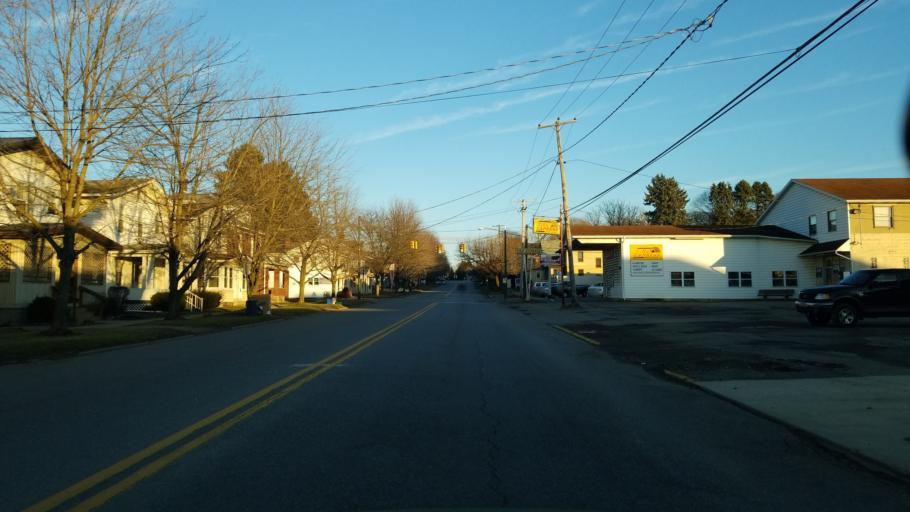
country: US
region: Pennsylvania
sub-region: Indiana County
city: Indiana
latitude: 40.6228
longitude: -79.1441
